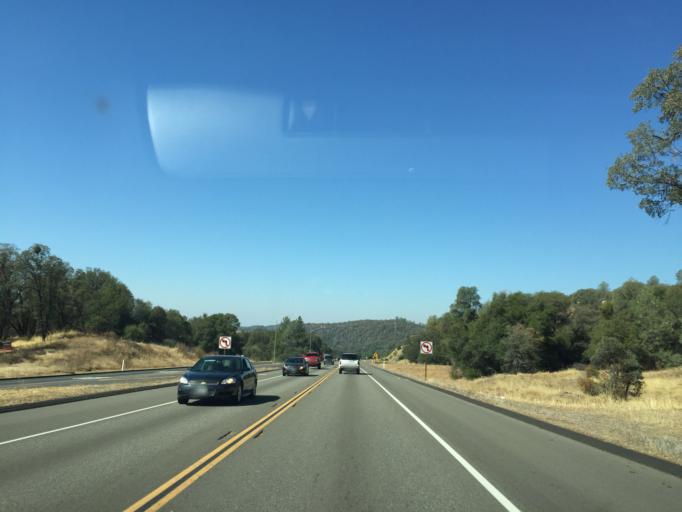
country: US
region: California
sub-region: Tuolumne County
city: East Sonora
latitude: 37.9806
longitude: -120.3193
